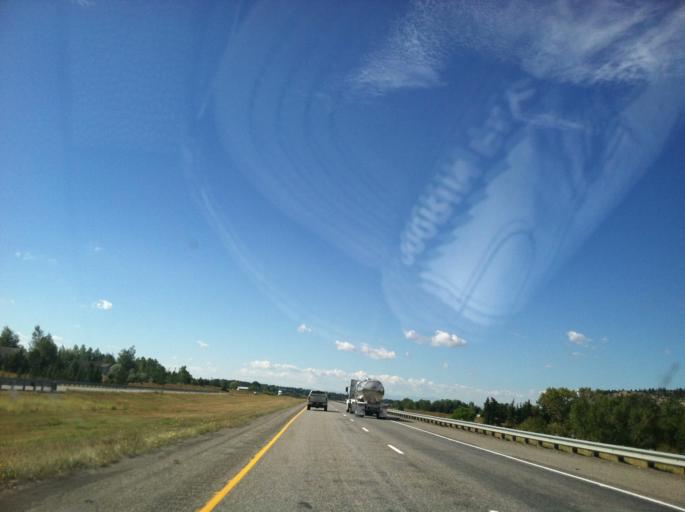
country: US
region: Montana
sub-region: Gallatin County
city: Bozeman
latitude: 45.6669
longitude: -110.9825
